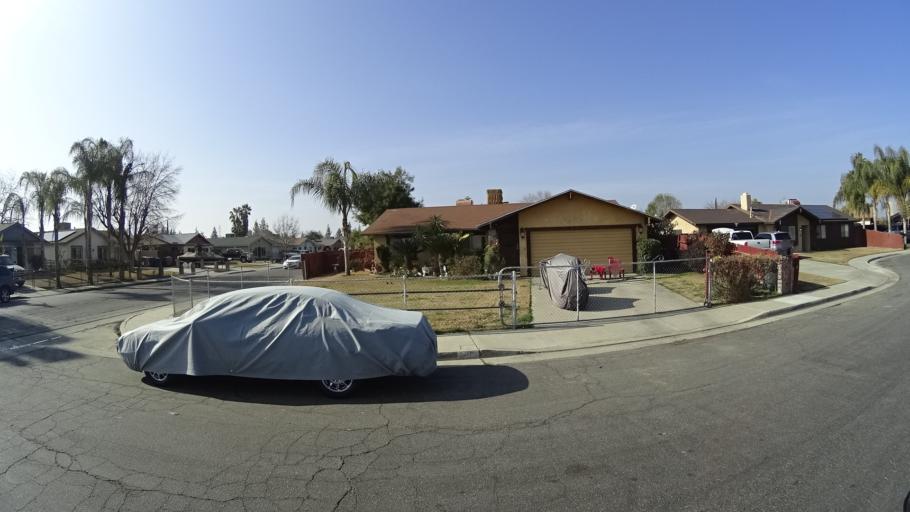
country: US
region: California
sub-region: Kern County
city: Bakersfield
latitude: 35.3210
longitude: -119.0585
